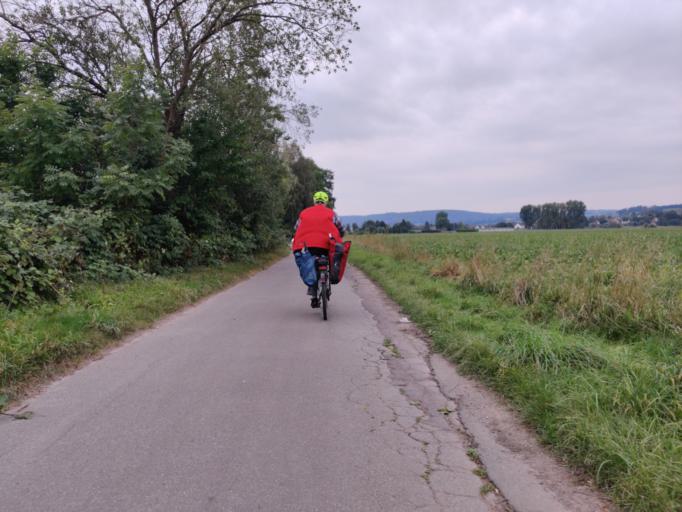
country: DE
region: Lower Saxony
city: Holzminden
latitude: 51.8421
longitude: 9.4448
